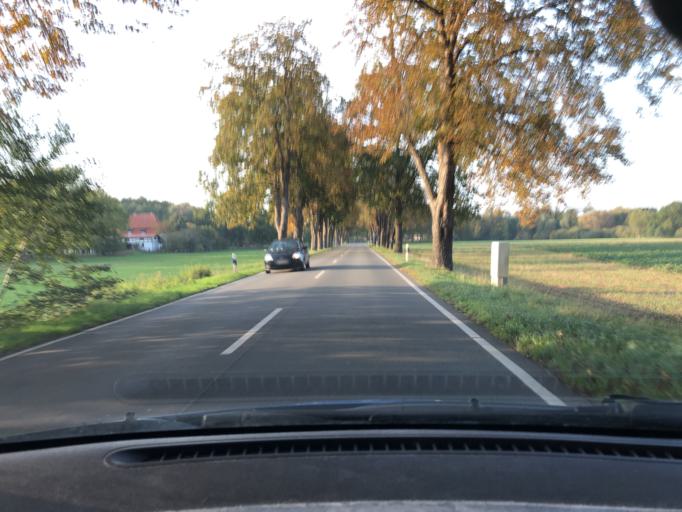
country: DE
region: Lower Saxony
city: Dannenberg
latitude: 53.1141
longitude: 11.0560
